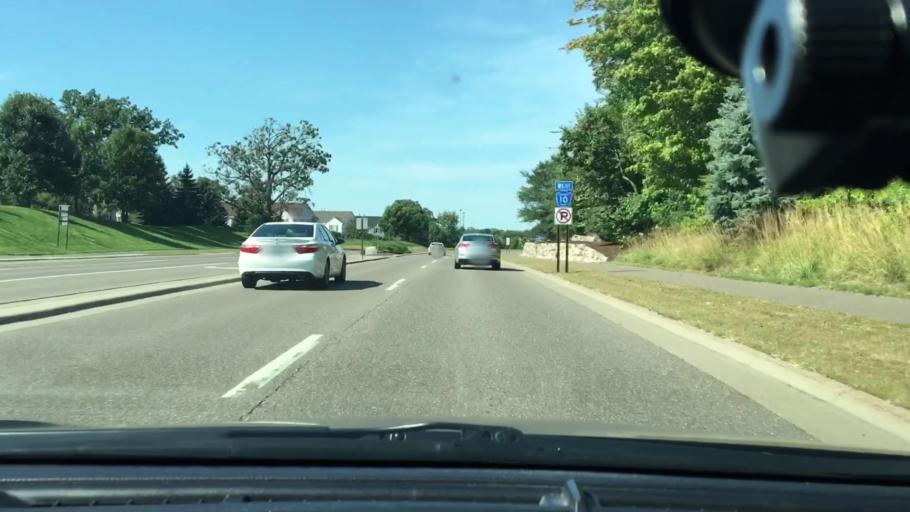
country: US
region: Minnesota
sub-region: Hennepin County
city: Corcoran
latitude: 45.0822
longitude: -93.5079
